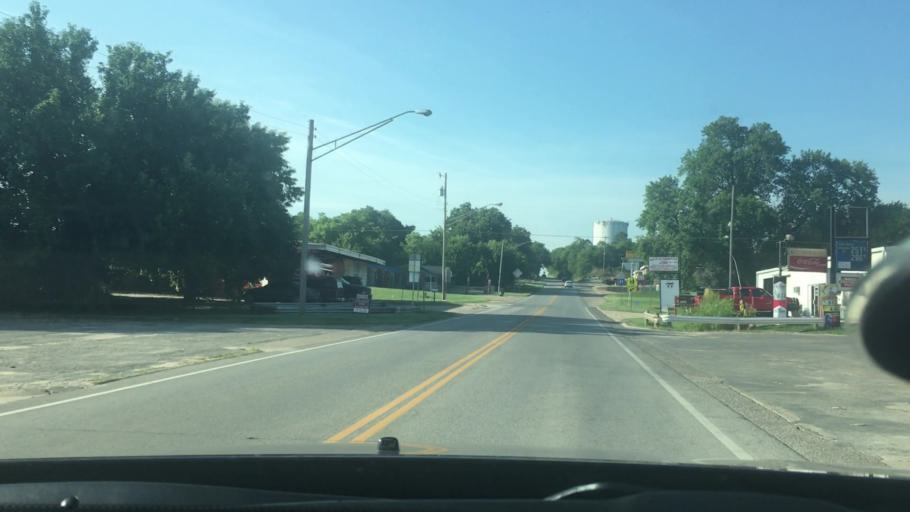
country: US
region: Oklahoma
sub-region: Garvin County
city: Pauls Valley
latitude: 34.7309
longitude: -97.2132
